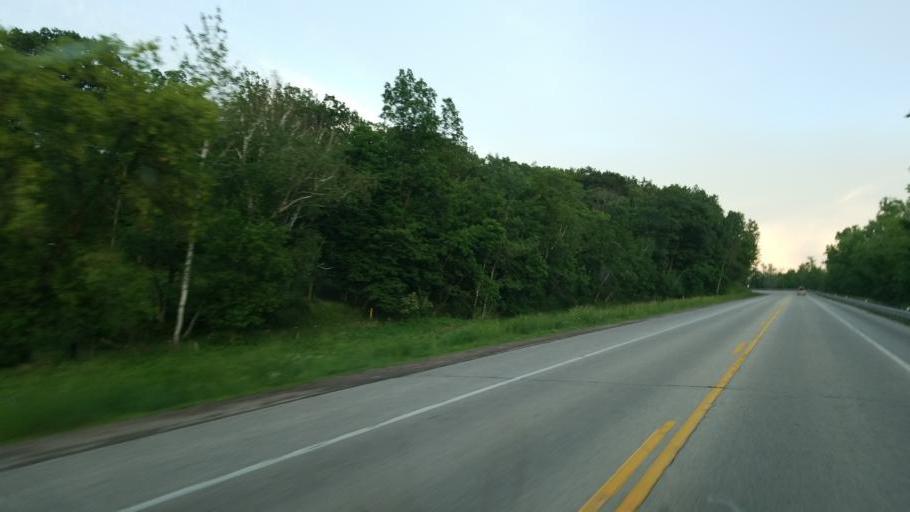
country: US
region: Wisconsin
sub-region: Monroe County
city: Tomah
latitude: 43.8180
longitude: -90.4372
